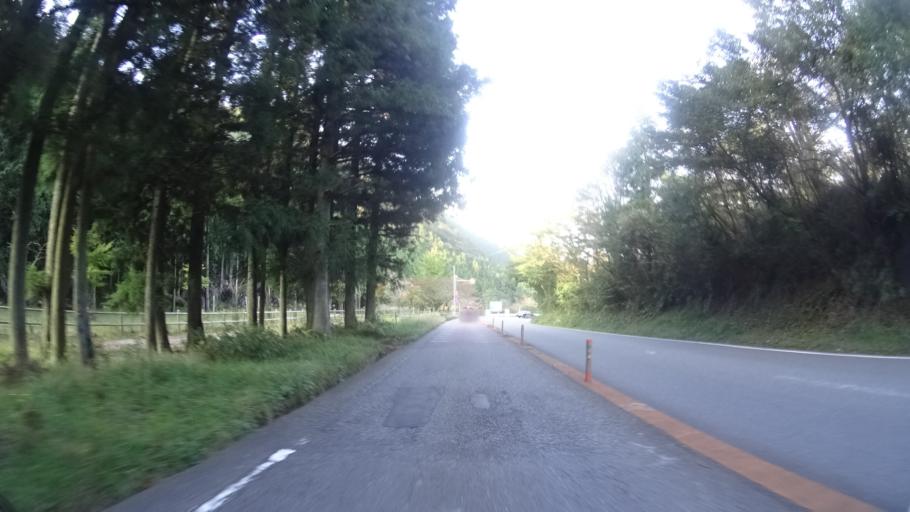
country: JP
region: Oita
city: Beppu
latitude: 33.2760
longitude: 131.4455
